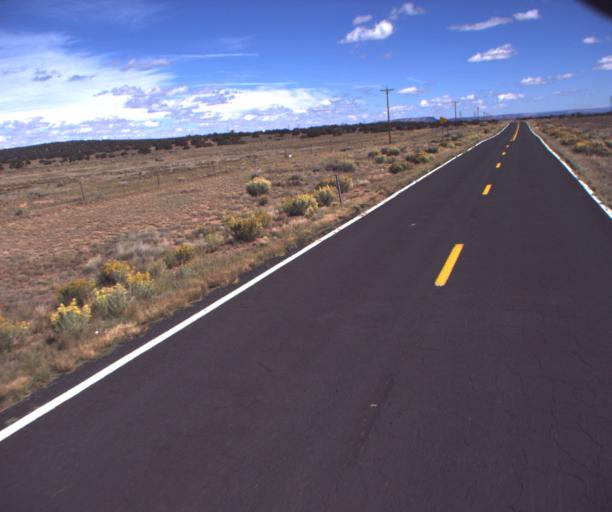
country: US
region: New Mexico
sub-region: McKinley County
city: Zuni Pueblo
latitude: 35.0136
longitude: -109.0616
